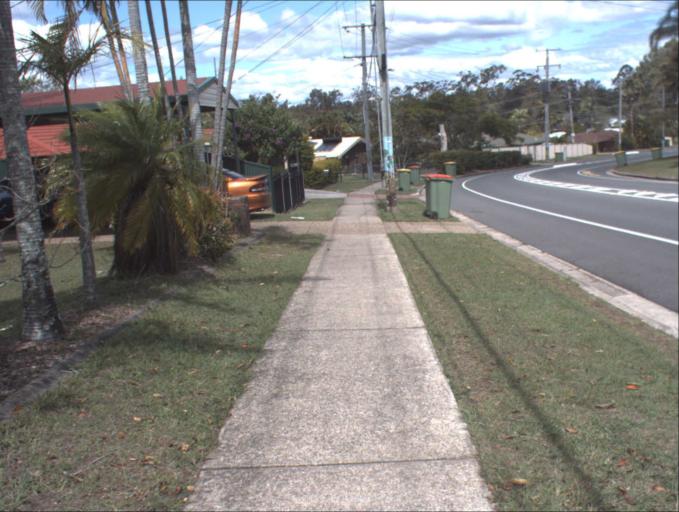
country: AU
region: Queensland
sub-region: Logan
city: Park Ridge South
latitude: -27.6668
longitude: 153.0233
